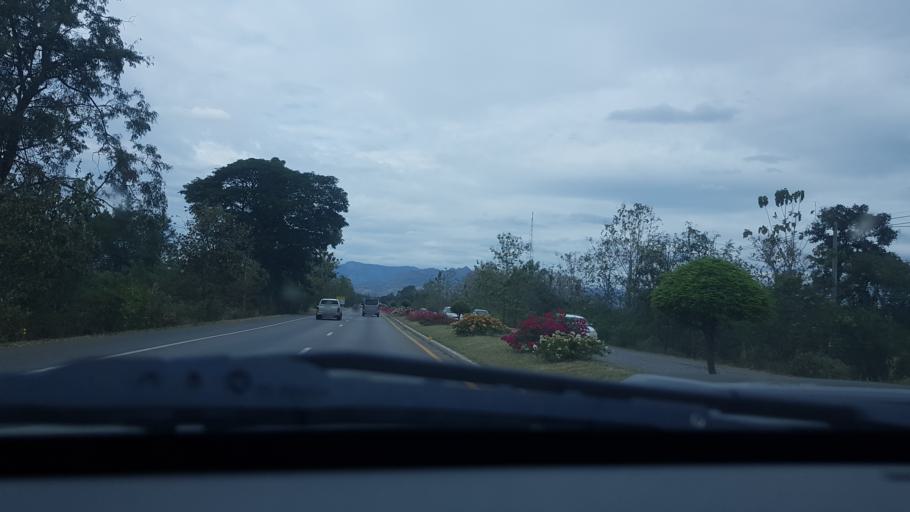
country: TH
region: Phetchabun
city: Phetchabun
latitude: 16.2415
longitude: 101.0761
